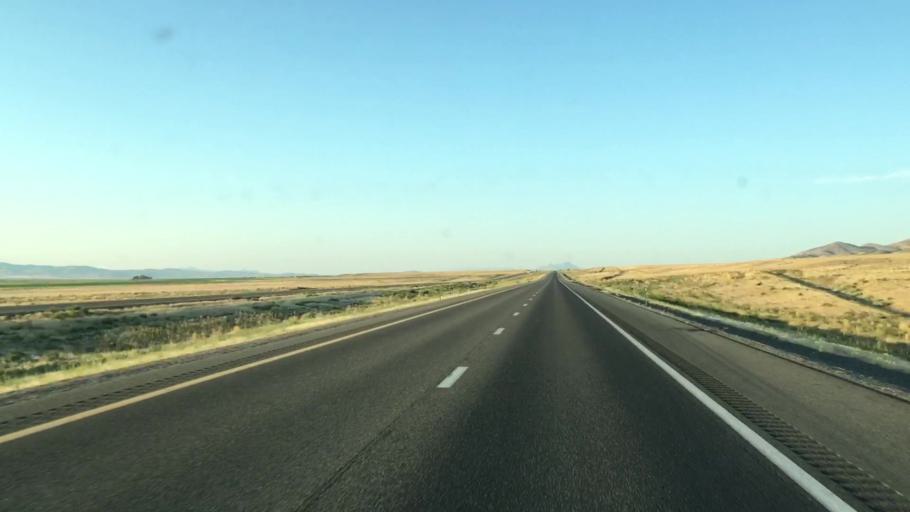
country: US
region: Nevada
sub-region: Humboldt County
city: Winnemucca
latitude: 40.7599
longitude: -118.0173
